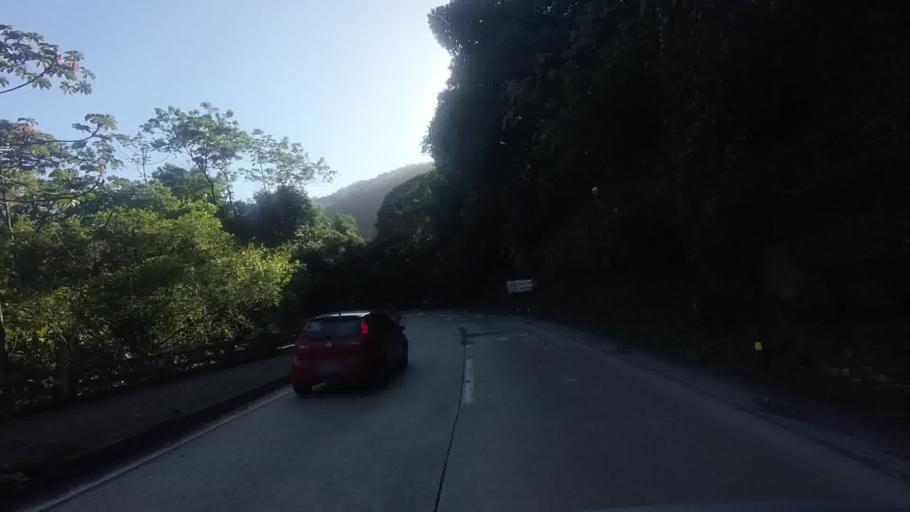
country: BR
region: Rio de Janeiro
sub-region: Petropolis
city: Petropolis
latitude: -22.5864
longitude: -43.2628
